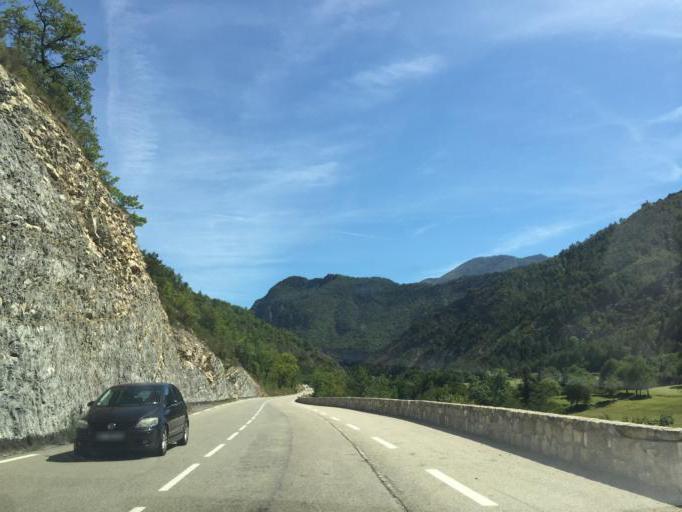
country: FR
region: Provence-Alpes-Cote d'Azur
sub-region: Departement des Alpes-Maritimes
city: Gilette
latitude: 43.9556
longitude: 7.1582
